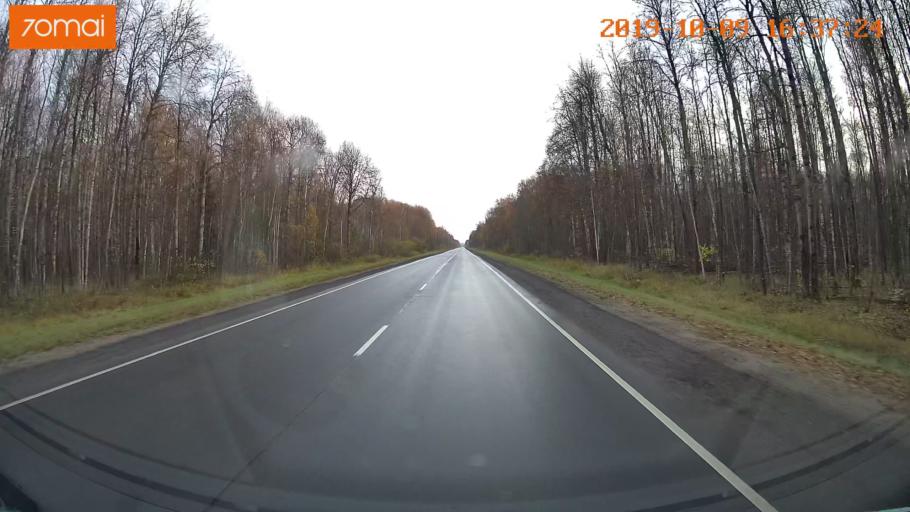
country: RU
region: Kostroma
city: Volgorechensk
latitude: 57.5275
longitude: 41.0242
